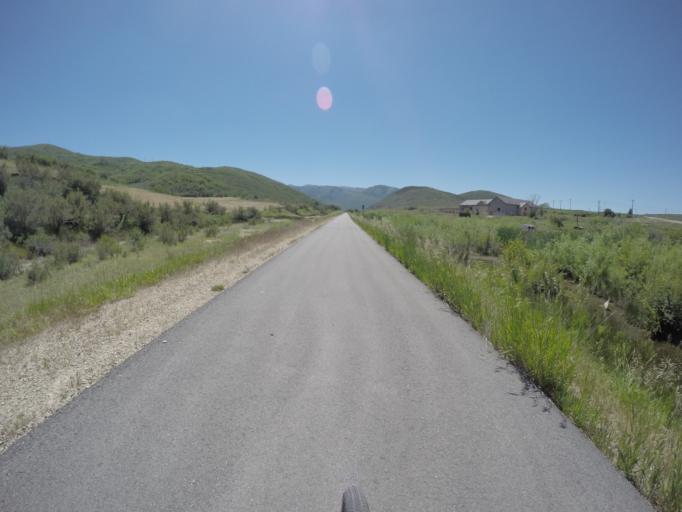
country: US
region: Utah
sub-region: Summit County
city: Park City
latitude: 40.6731
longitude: -111.4659
